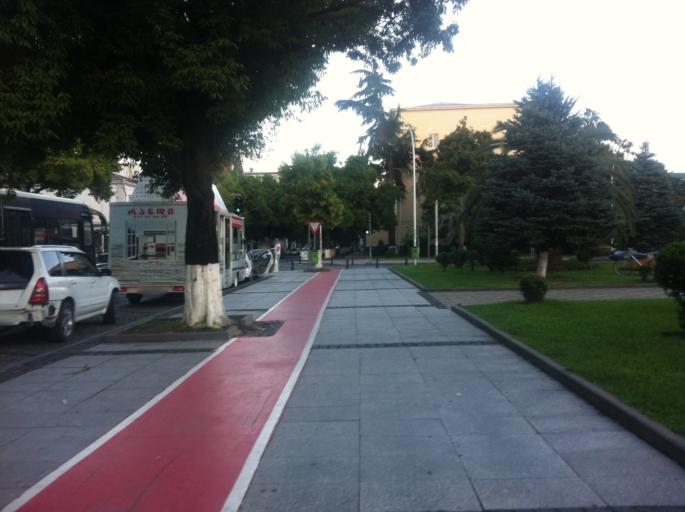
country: GE
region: Ajaria
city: Batumi
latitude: 41.6495
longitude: 41.6354
